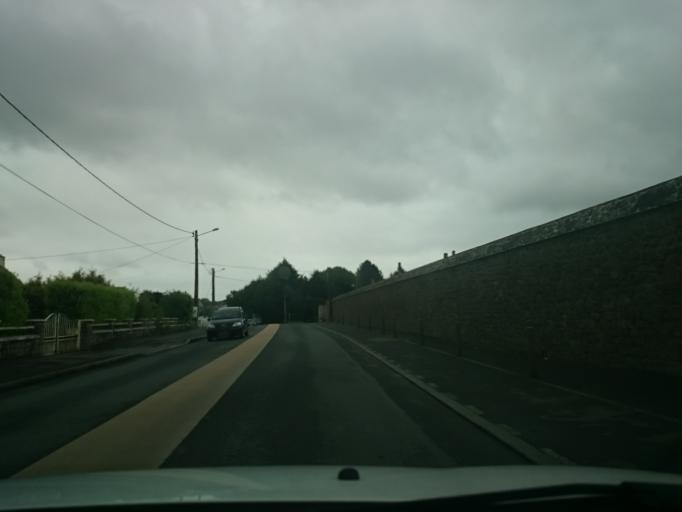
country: FR
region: Brittany
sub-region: Departement des Cotes-d'Armor
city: Guingamp
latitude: 48.5525
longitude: -3.1491
